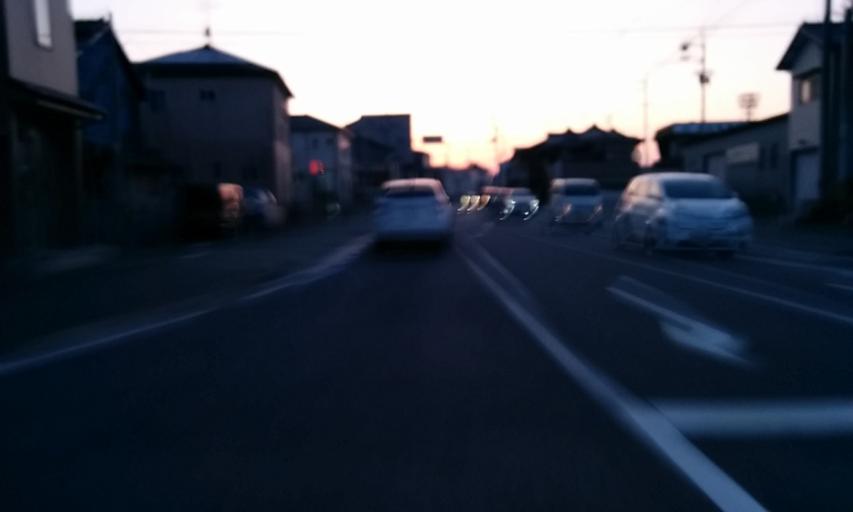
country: JP
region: Ehime
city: Ozu
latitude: 33.6151
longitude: 132.4832
